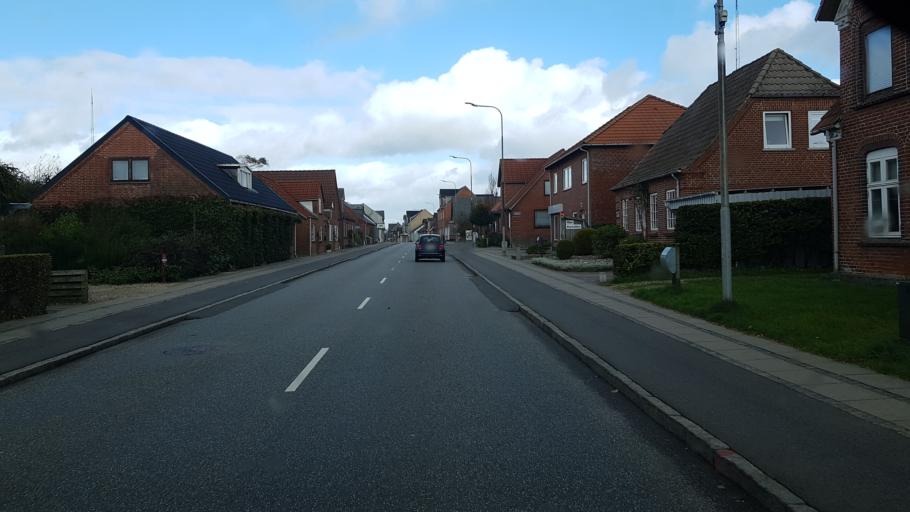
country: DK
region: South Denmark
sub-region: Vejen Kommune
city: Holsted
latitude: 55.4811
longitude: 8.9107
